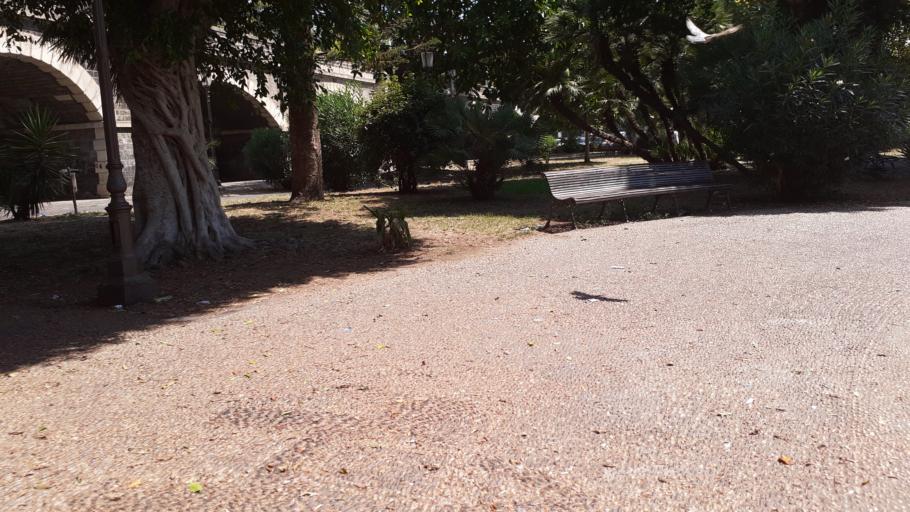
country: IT
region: Sicily
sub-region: Catania
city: Catania
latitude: 37.5012
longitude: 15.0877
